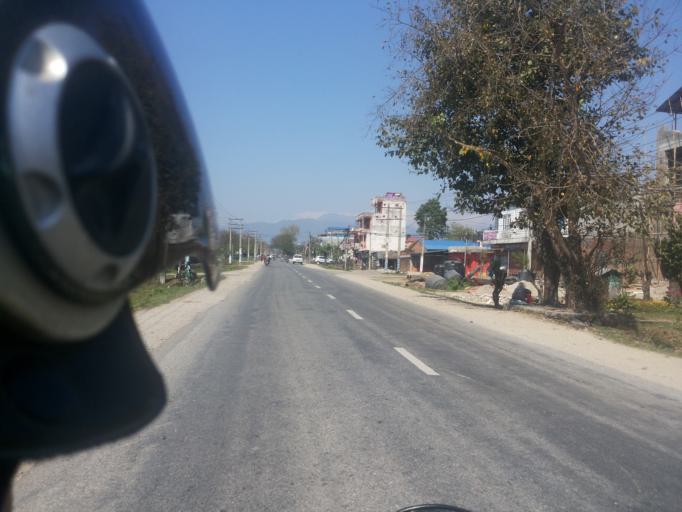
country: NP
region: Central Region
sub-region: Narayani Zone
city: Bharatpur
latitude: 27.6773
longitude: 84.4390
